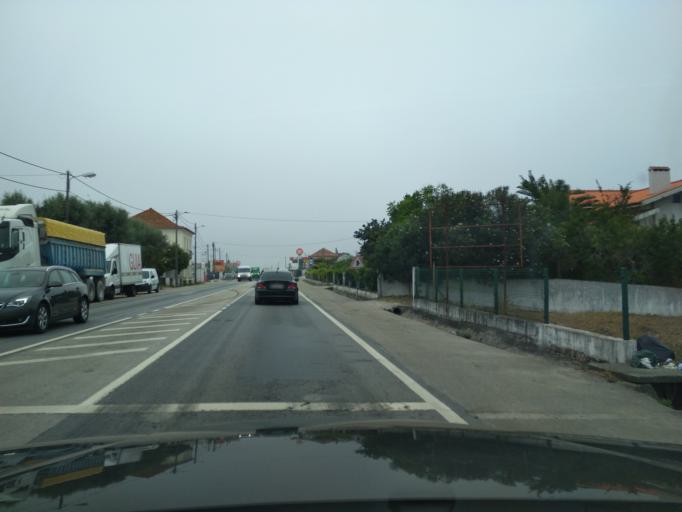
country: PT
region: Aveiro
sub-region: Mealhada
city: Pampilhosa do Botao
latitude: 40.3056
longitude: -8.4484
